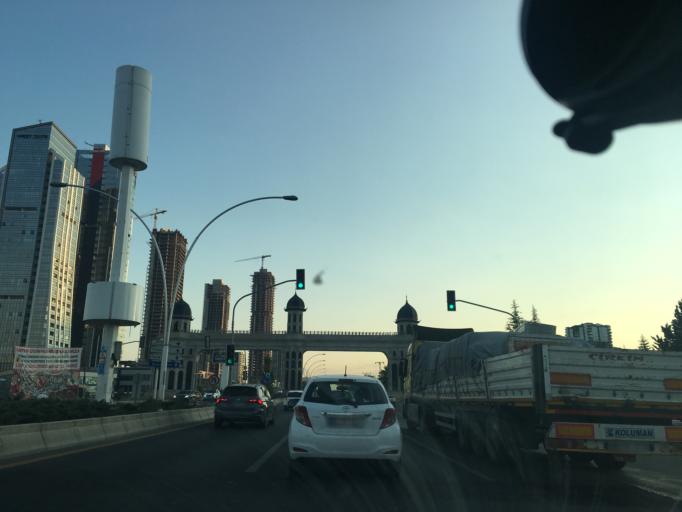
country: TR
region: Ankara
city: Etimesgut
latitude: 39.8812
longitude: 32.6581
